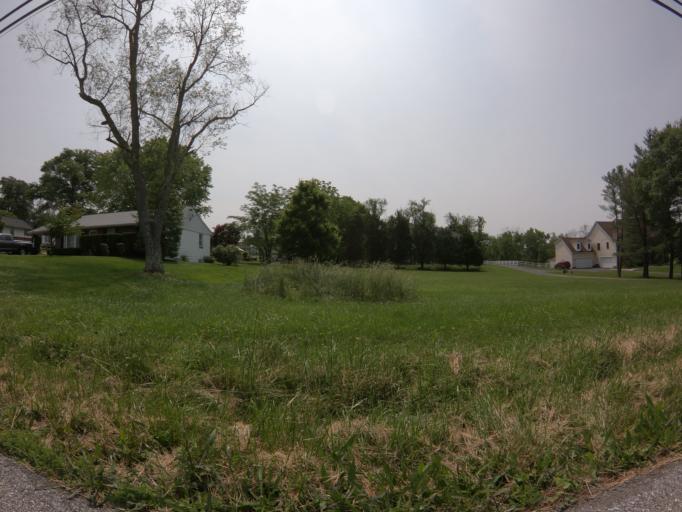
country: US
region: Maryland
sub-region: Howard County
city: Ellicott City
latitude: 39.2377
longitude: -76.8044
